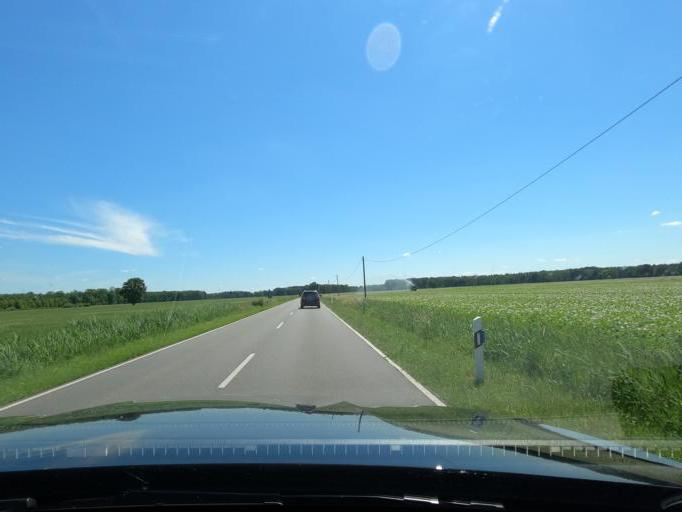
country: DE
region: Lower Saxony
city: Hohne
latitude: 52.5783
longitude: 10.3763
